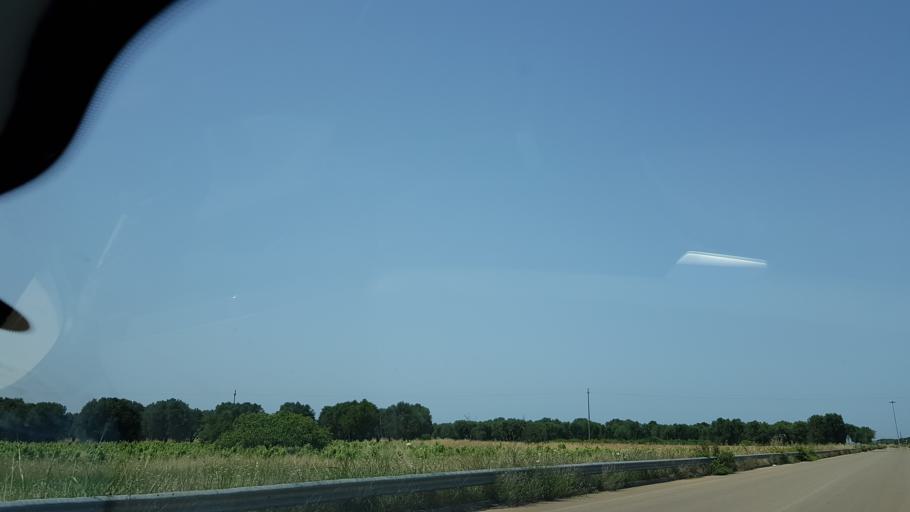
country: IT
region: Apulia
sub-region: Provincia di Brindisi
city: Mesagne
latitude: 40.5545
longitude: 17.8348
